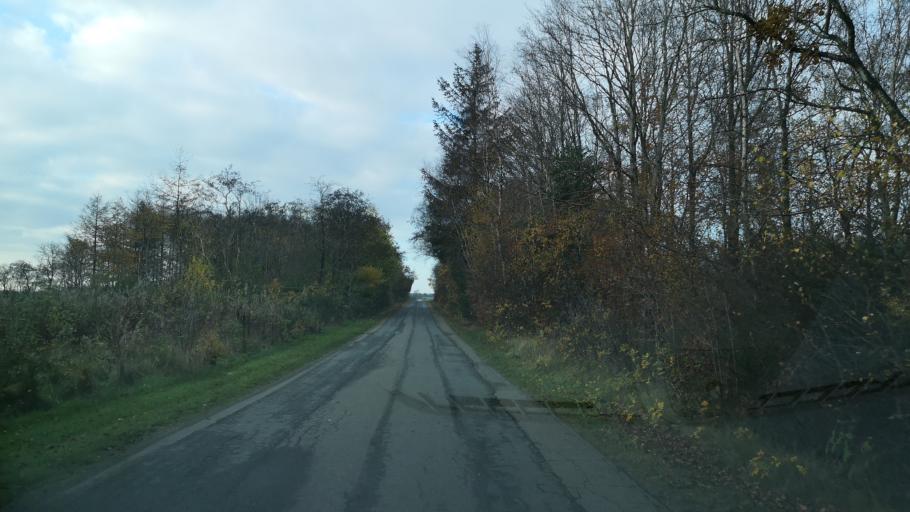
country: DK
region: Central Jutland
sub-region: Ringkobing-Skjern Kommune
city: Videbaek
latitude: 56.0403
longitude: 8.5973
